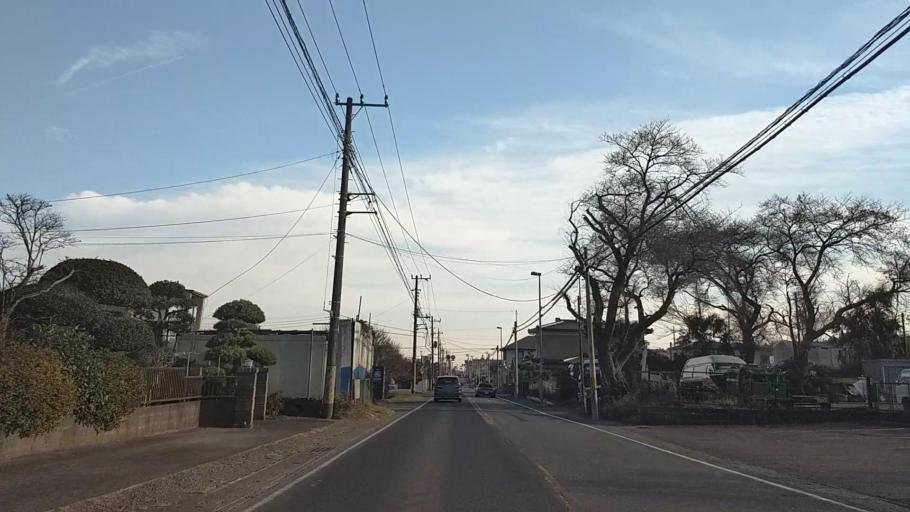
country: JP
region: Kanagawa
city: Zama
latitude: 35.5157
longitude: 139.2971
